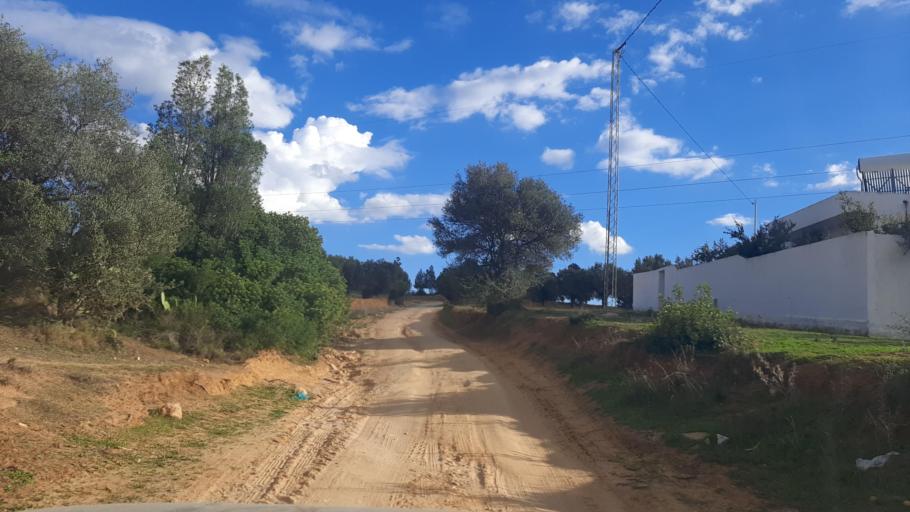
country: TN
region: Nabul
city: Bu `Urqub
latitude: 36.4397
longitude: 10.5085
